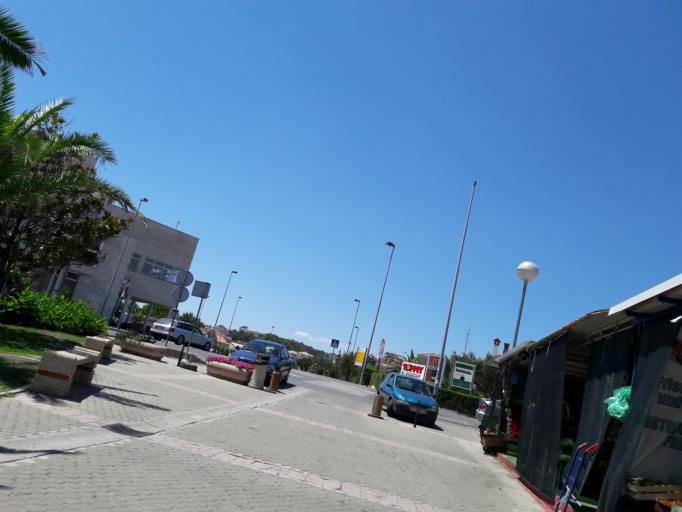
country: HR
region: Primorsko-Goranska
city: Banjol
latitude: 44.7618
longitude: 14.7593
